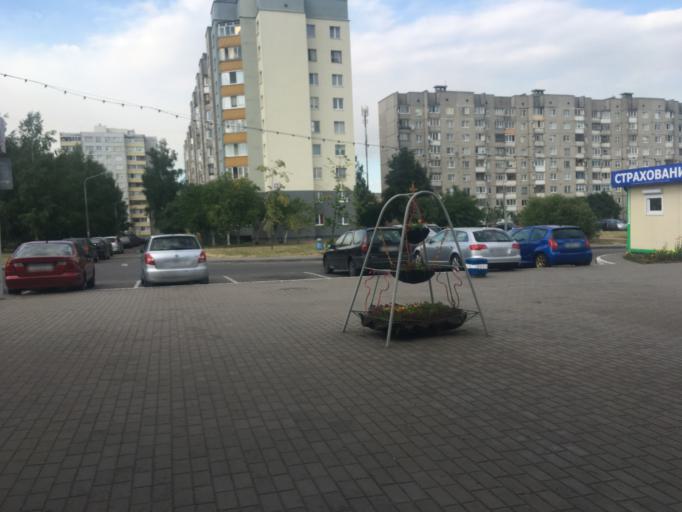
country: BY
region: Grodnenskaya
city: Hrodna
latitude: 53.6488
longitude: 23.8364
